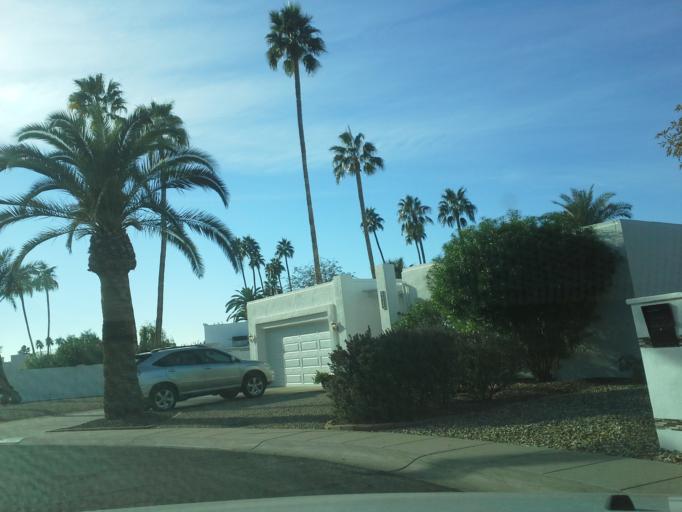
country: US
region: Arizona
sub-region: Maricopa County
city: Glendale
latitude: 33.6118
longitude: -112.0692
